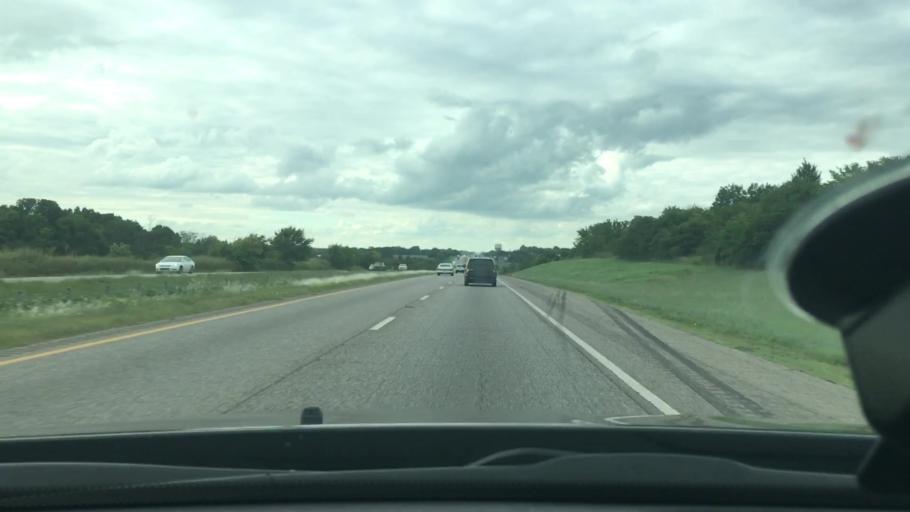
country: US
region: Oklahoma
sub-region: Cleveland County
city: Noble
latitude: 35.0983
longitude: -97.4258
